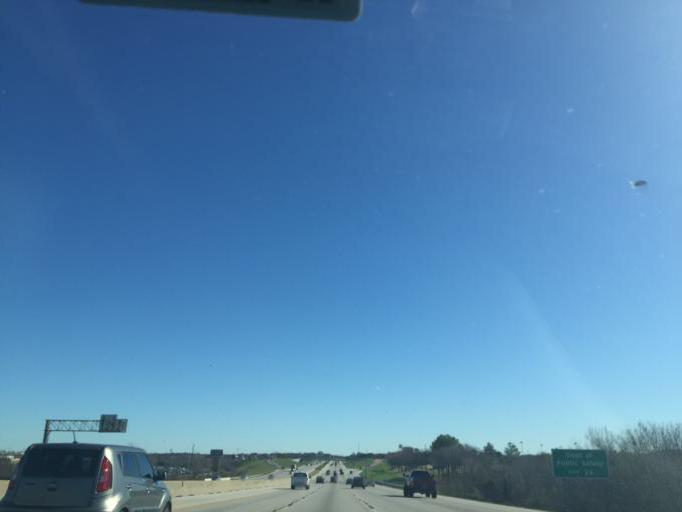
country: US
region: Texas
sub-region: Tarrant County
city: Pantego
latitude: 32.7601
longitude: -97.1755
